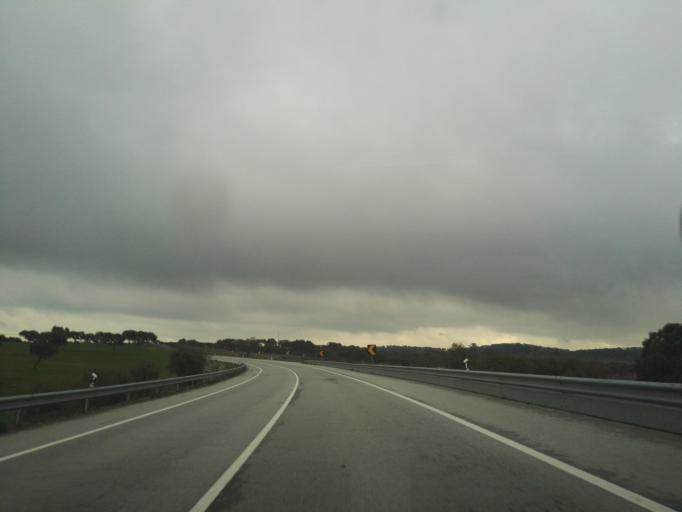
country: PT
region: Portalegre
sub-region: Portalegre
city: Urra
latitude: 39.2124
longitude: -7.3777
